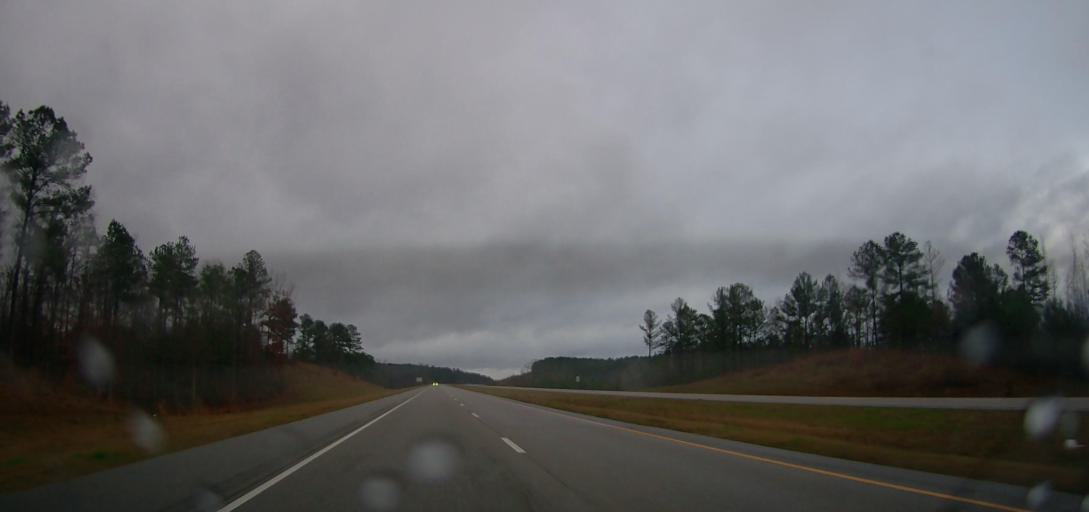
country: US
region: Alabama
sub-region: Bibb County
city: Centreville
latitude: 32.9562
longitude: -87.1235
